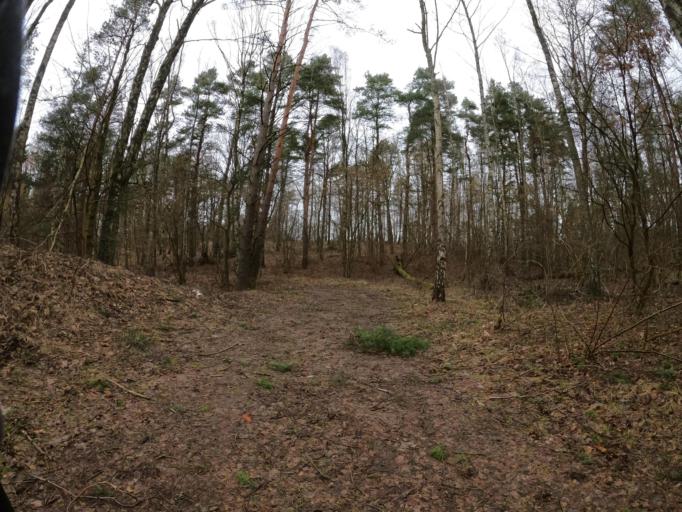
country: PL
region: Greater Poland Voivodeship
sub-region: Powiat zlotowski
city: Sypniewo
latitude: 53.4952
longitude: 16.5614
